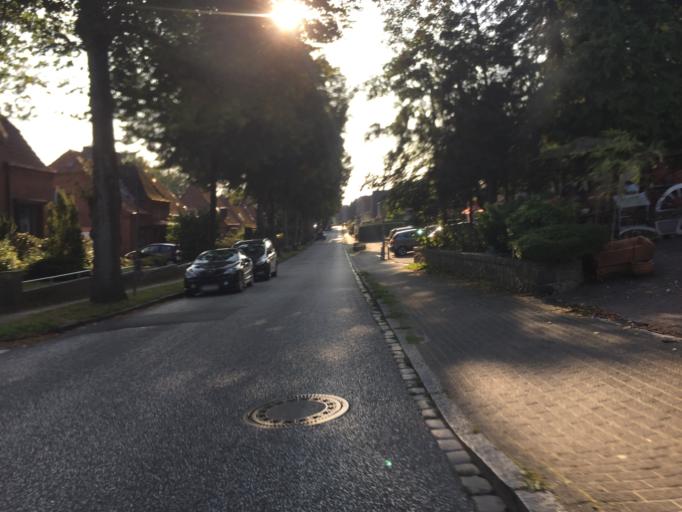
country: DE
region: Schleswig-Holstein
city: Itzehoe
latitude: 53.9267
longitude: 9.5362
